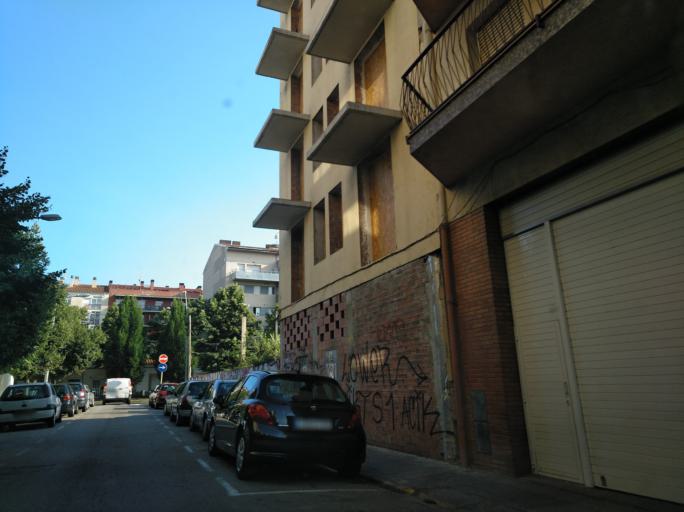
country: ES
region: Catalonia
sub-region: Provincia de Girona
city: Salt
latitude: 41.9734
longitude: 2.7928
